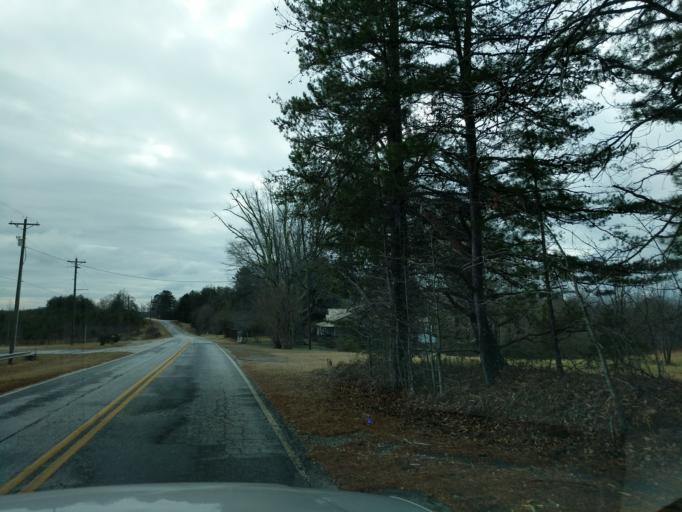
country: US
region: Georgia
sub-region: Rabun County
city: Clayton
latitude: 34.7871
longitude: -83.2503
